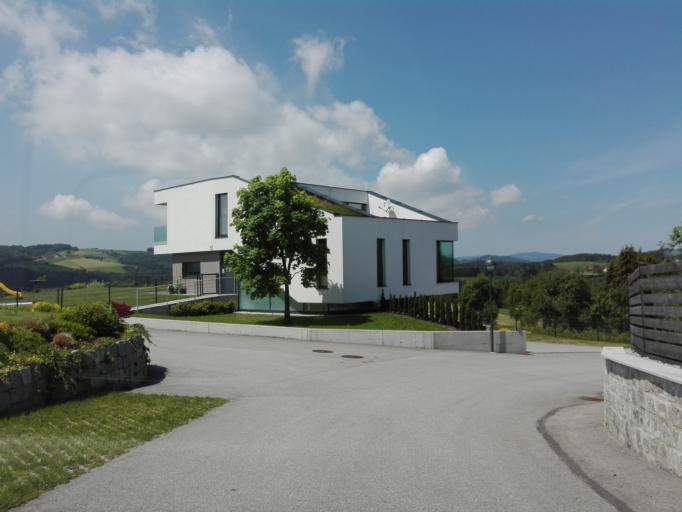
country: AT
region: Upper Austria
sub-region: Politischer Bezirk Rohrbach
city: Atzesberg
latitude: 48.4104
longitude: 13.9120
